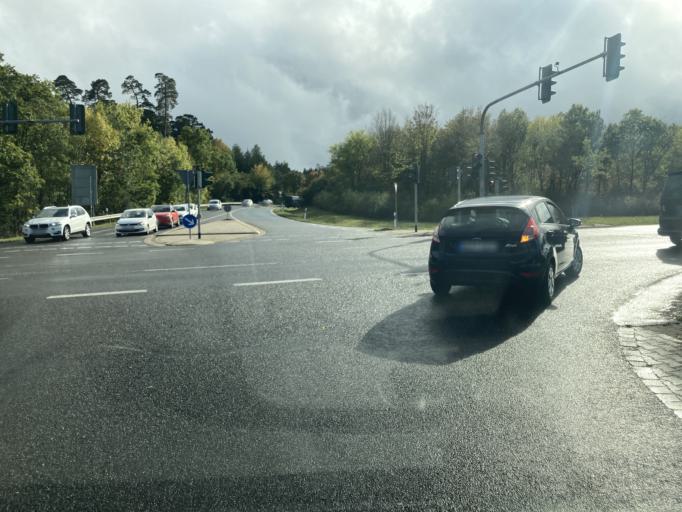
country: DE
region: Hesse
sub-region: Regierungsbezirk Darmstadt
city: Wehrheim
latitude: 50.2840
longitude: 8.5694
